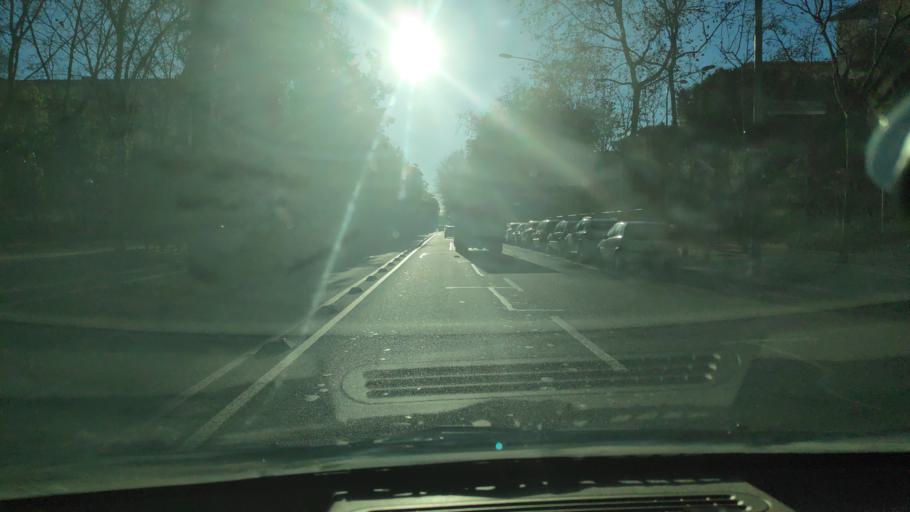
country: ES
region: Catalonia
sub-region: Provincia de Barcelona
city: Sant Marti
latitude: 41.4151
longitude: 2.2140
